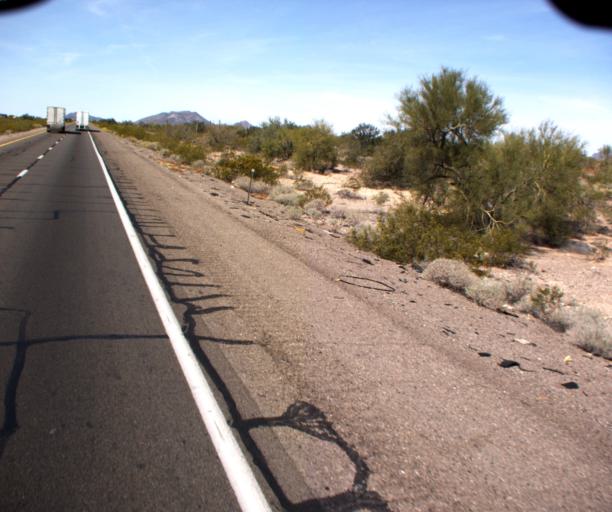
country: US
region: Arizona
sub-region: La Paz County
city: Quartzsite
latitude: 33.6512
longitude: -113.9203
